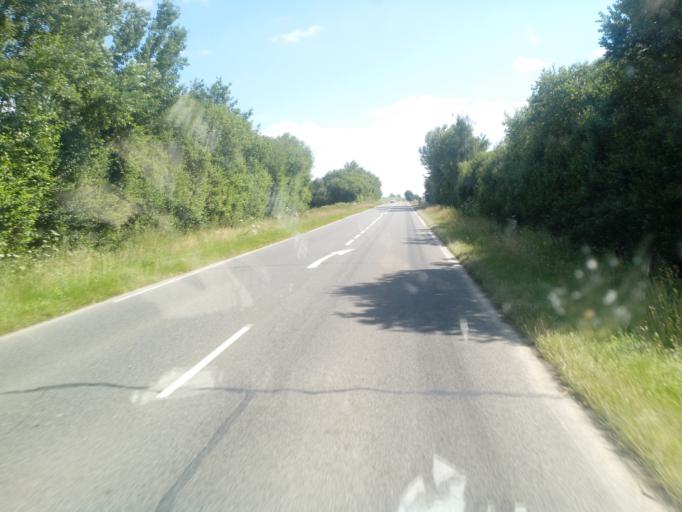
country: FR
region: Brittany
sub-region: Departement d'Ille-et-Vilaine
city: Acigne
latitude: 48.1418
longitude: -1.5164
